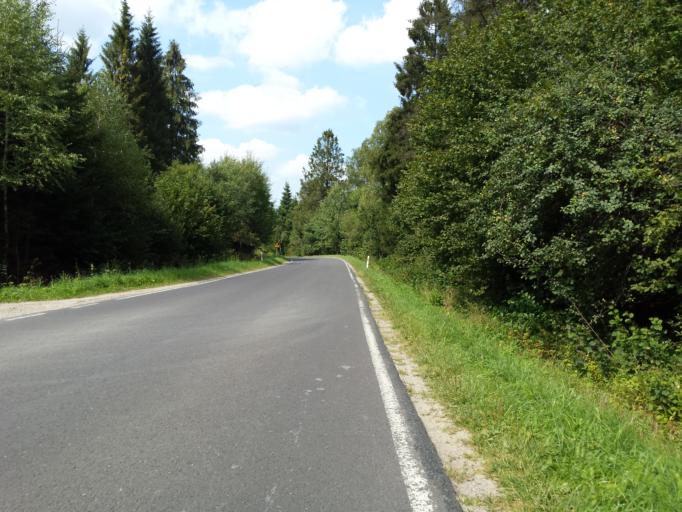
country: PL
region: Subcarpathian Voivodeship
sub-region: Powiat leski
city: Cisna
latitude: 49.1710
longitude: 22.4461
